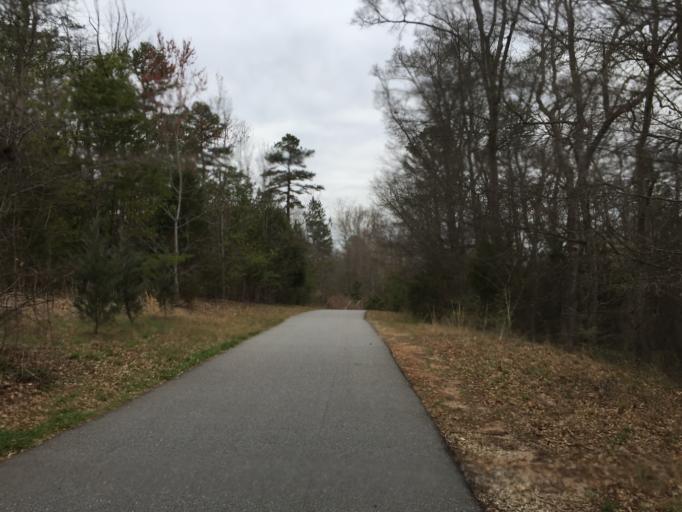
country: US
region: South Carolina
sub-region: Greenville County
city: Mauldin
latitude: 34.7702
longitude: -82.3516
